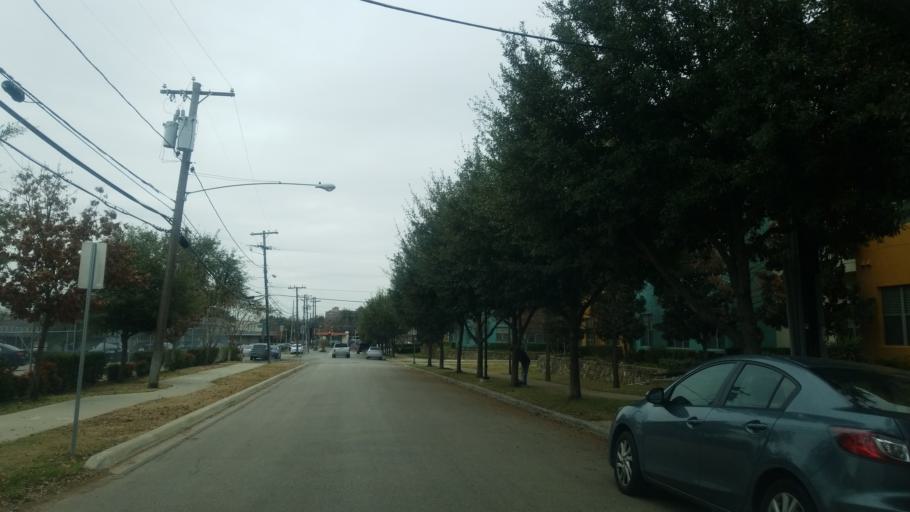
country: US
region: Texas
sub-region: Dallas County
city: Highland Park
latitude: 32.8255
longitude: -96.8184
